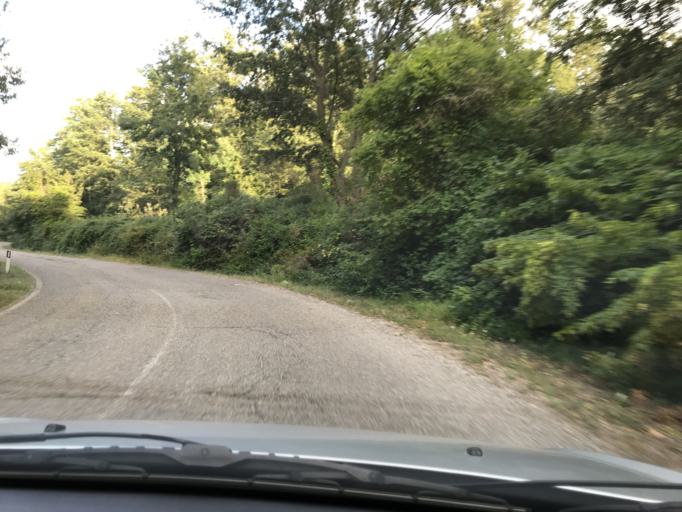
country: IT
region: Umbria
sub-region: Provincia di Terni
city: Guardea
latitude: 42.6476
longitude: 12.3520
